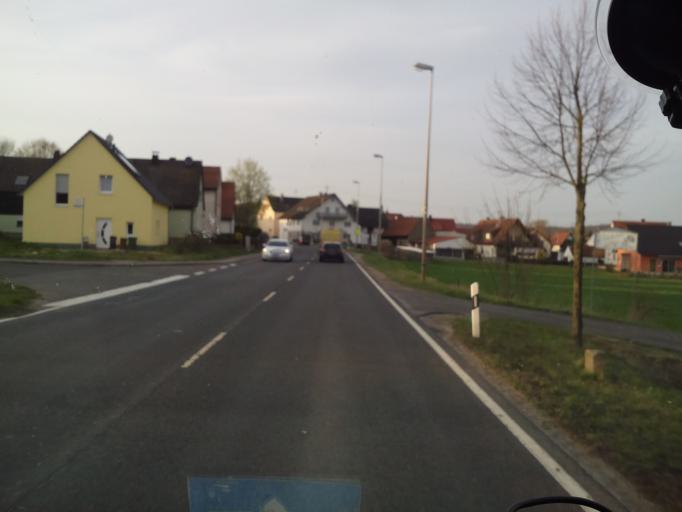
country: DE
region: Bavaria
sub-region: Upper Franconia
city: Reckendorf
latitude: 50.0156
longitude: 10.8274
